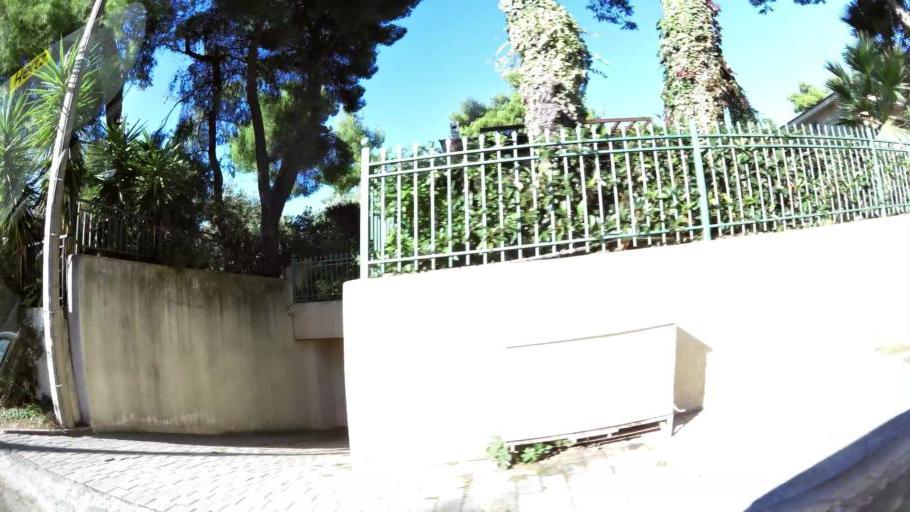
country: GR
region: Attica
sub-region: Nomarchia Anatolikis Attikis
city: Drosia
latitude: 38.1126
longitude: 23.8510
